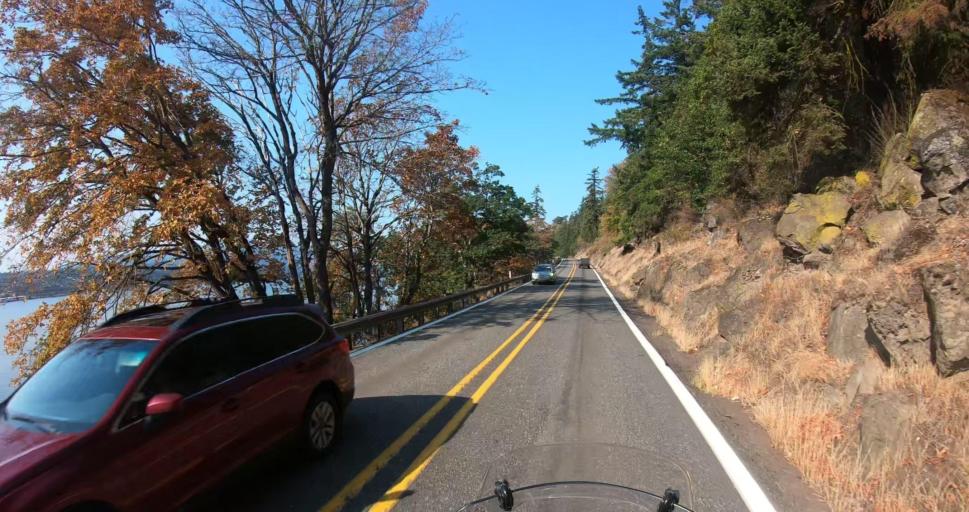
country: US
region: Washington
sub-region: Klickitat County
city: White Salmon
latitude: 45.7272
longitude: -121.5085
